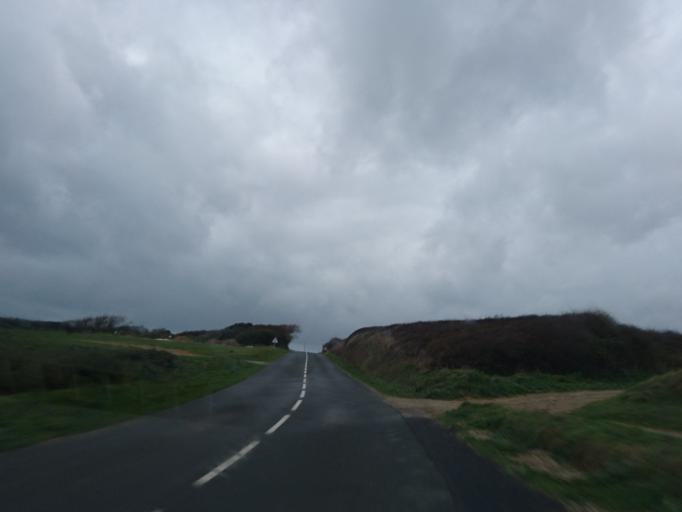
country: FR
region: Brittany
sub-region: Departement du Finistere
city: Le Conquet
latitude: 48.3479
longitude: -4.7688
